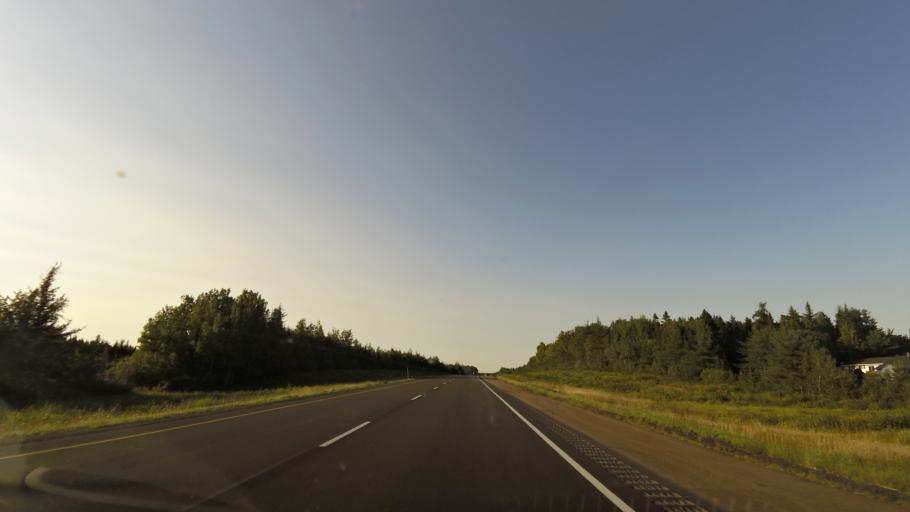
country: CA
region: New Brunswick
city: Dieppe
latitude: 46.0757
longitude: -64.5920
